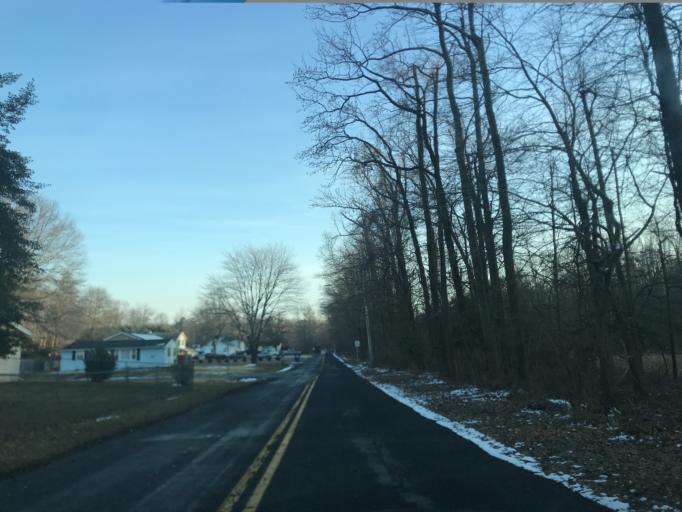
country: US
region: Maryland
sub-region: Harford County
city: Riverside
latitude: 39.4378
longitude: -76.2564
